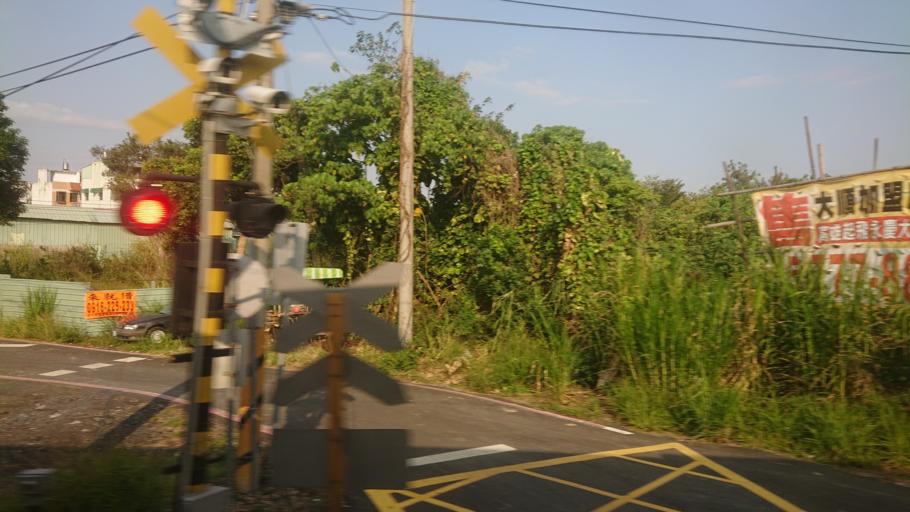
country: TW
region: Taiwan
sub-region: Chiayi
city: Jiayi Shi
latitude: 23.5913
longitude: 120.4464
